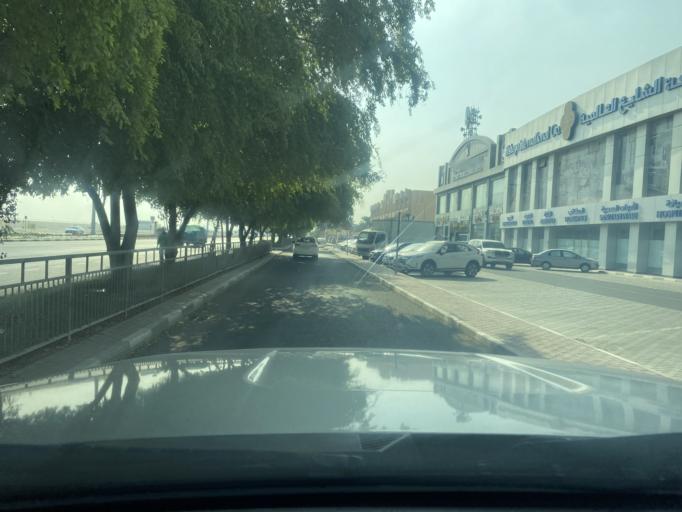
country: QA
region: Baladiyat ad Dawhah
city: Doha
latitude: 25.2403
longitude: 51.5709
